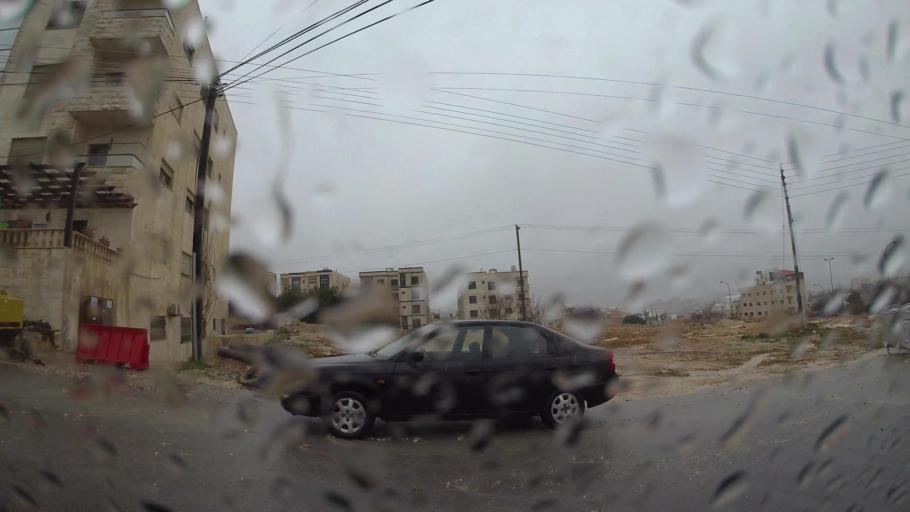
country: JO
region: Amman
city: Al Jubayhah
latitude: 32.0283
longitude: 35.8904
